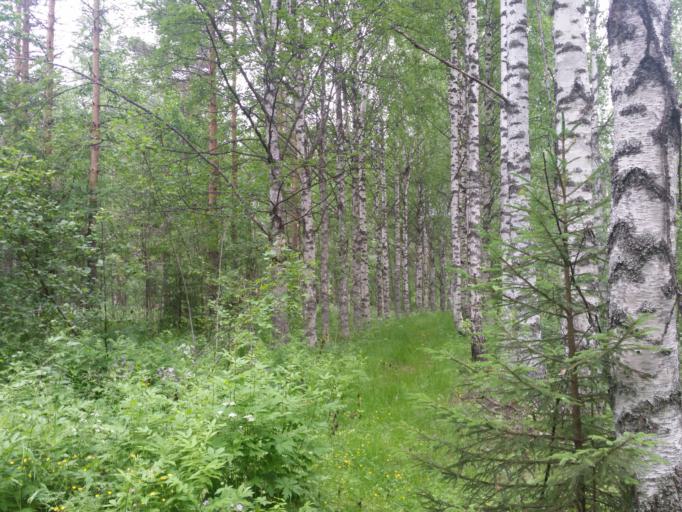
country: FI
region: Northern Savo
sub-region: Koillis-Savo
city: Kaavi
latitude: 62.9820
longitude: 28.7632
